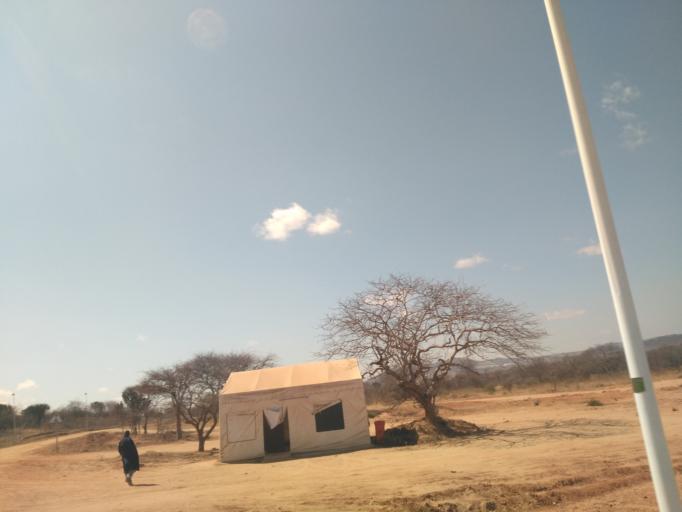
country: TZ
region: Dodoma
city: Dodoma
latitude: -6.1559
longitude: 35.7584
